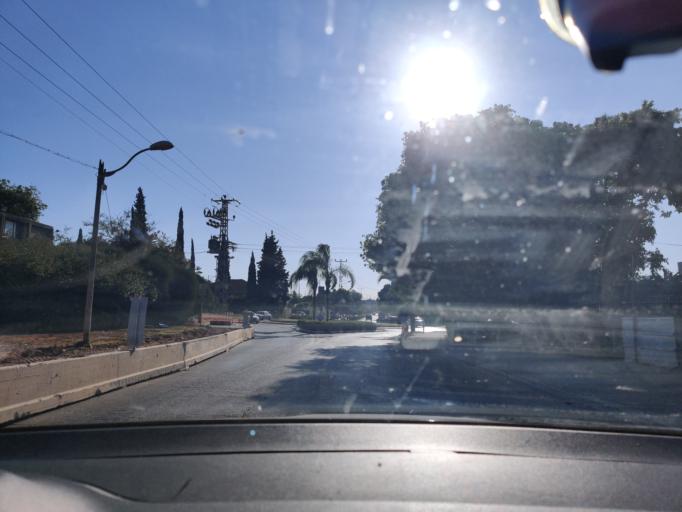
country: IL
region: Haifa
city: Hadera
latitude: 32.4713
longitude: 34.9636
